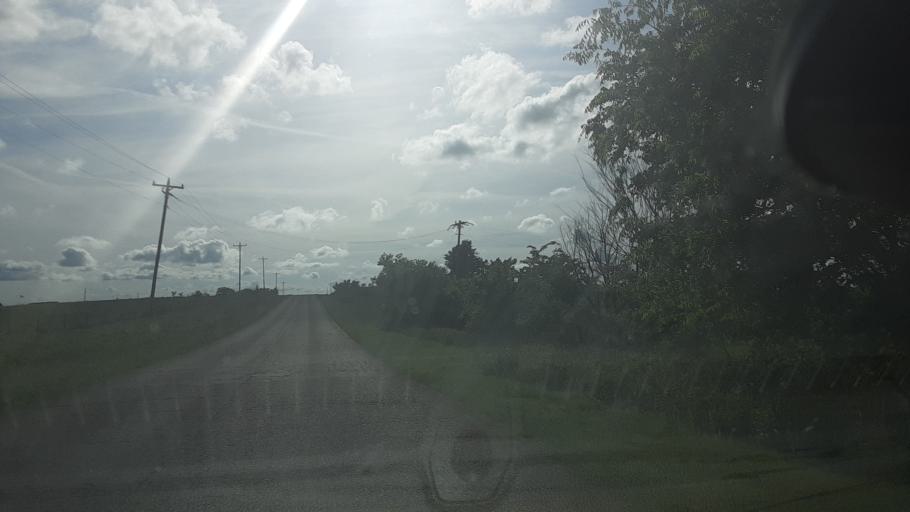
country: US
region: Oklahoma
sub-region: Logan County
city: Langston
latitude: 36.0579
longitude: -97.3777
